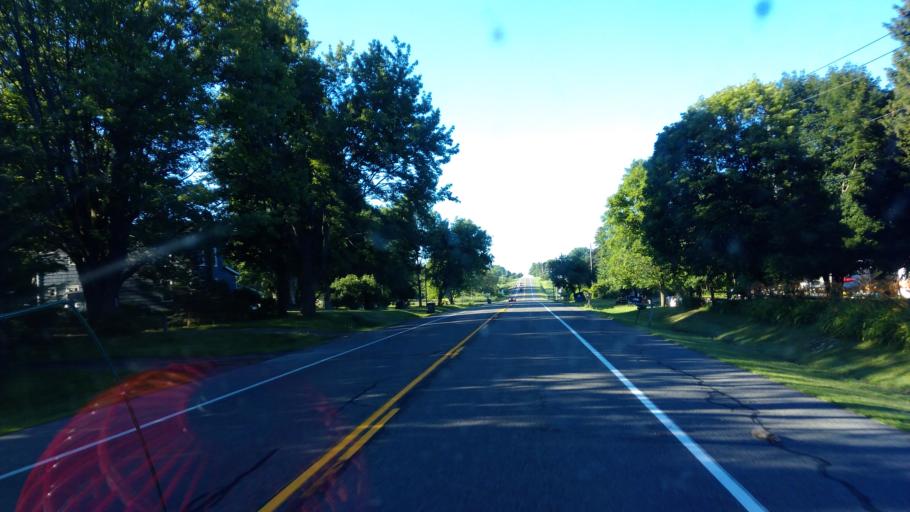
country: US
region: New York
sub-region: Ontario County
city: Phelps
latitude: 42.9782
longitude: -76.9778
